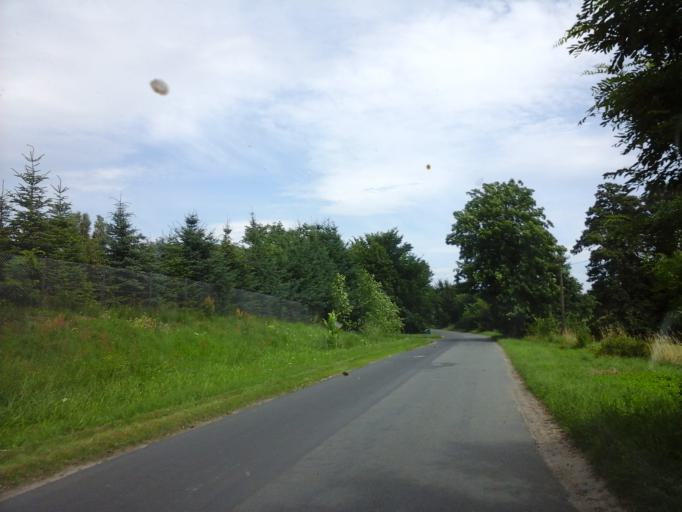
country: PL
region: Lubusz
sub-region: Powiat strzelecko-drezdenecki
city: Dobiegniew
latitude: 53.0545
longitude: 15.7551
